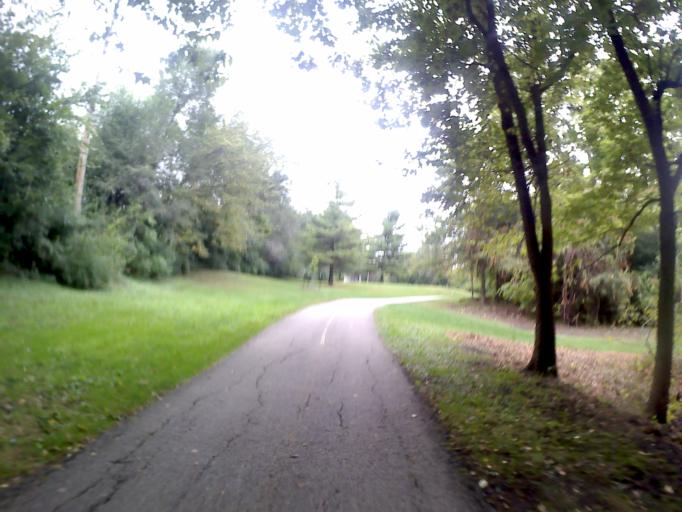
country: US
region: Illinois
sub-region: Kane County
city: Aurora
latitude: 41.7806
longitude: -88.3141
